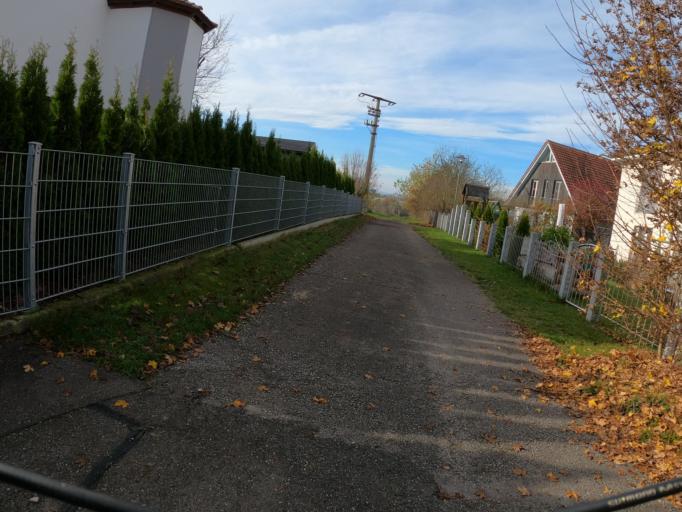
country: DE
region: Bavaria
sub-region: Swabia
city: Leipheim
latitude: 48.4308
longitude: 10.1875
